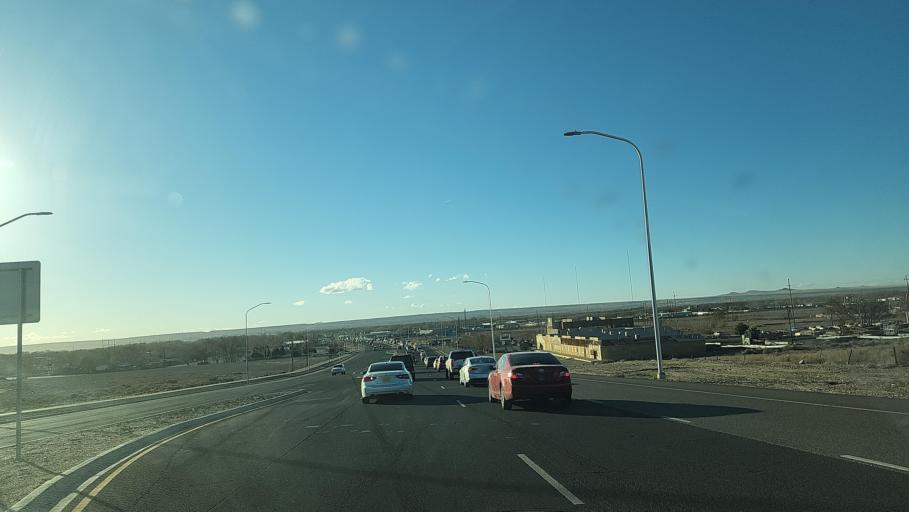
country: US
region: New Mexico
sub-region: Bernalillo County
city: South Valley
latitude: 35.0259
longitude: -106.6492
